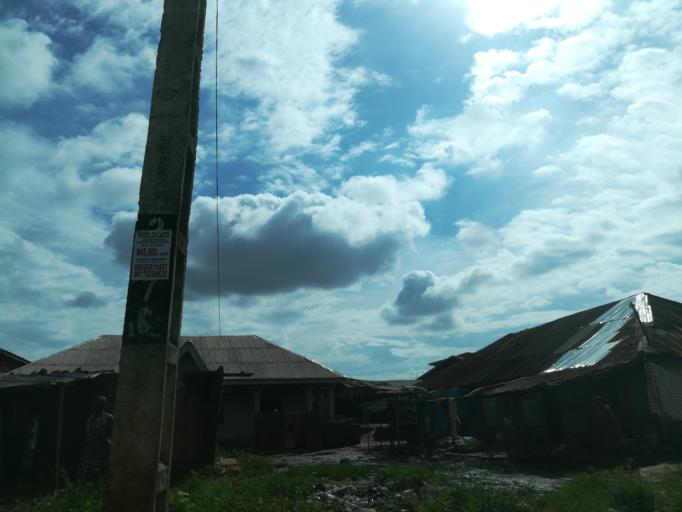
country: NG
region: Lagos
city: Ikorodu
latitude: 6.5932
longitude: 3.5176
